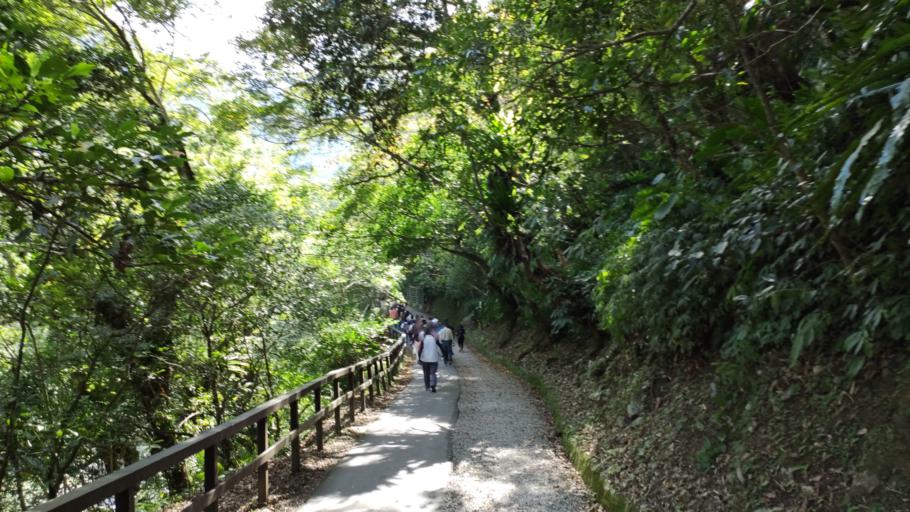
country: TW
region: Taiwan
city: Daxi
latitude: 24.8278
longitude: 121.4464
